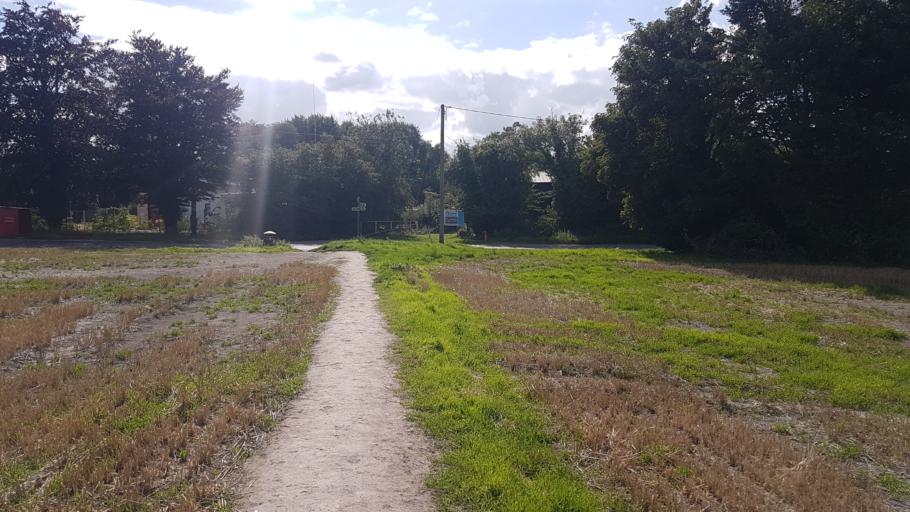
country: GB
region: England
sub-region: Suffolk
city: Exning
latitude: 52.2681
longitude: 0.3222
